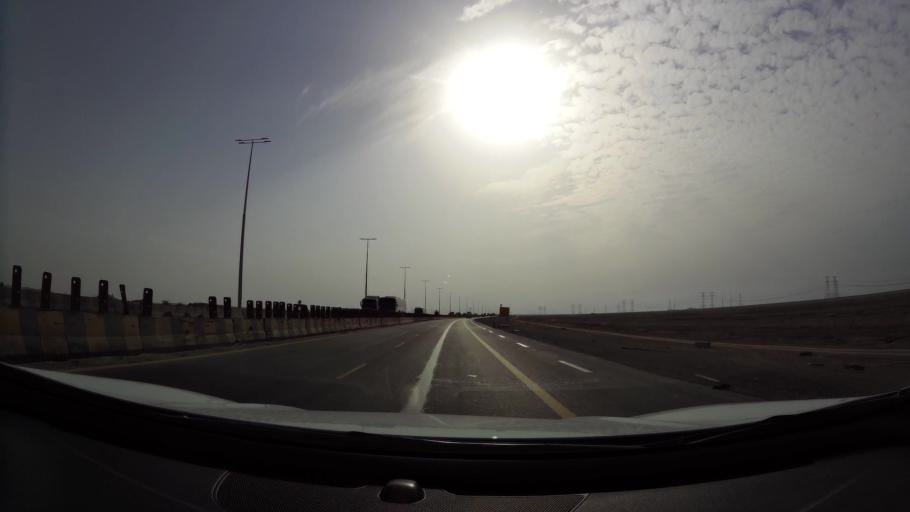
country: AE
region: Abu Dhabi
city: Abu Dhabi
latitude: 24.2325
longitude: 54.4567
